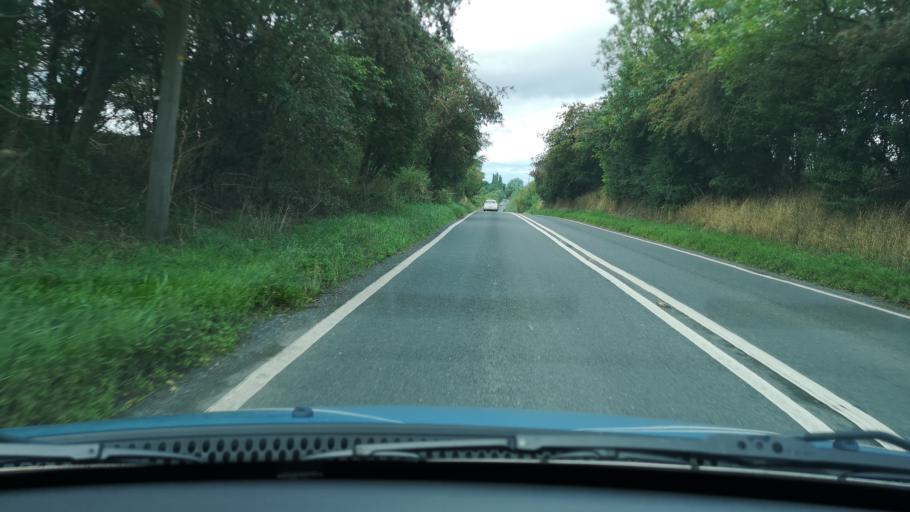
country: GB
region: England
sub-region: City and Borough of Wakefield
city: Low Ackworth
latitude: 53.6343
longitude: -1.3248
